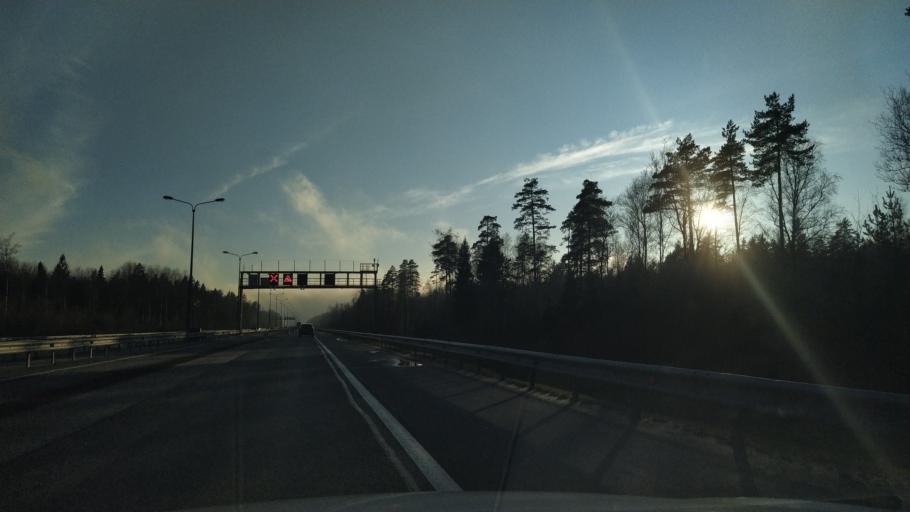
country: RU
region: St.-Petersburg
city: Lisiy Nos
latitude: 60.0477
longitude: 30.0603
